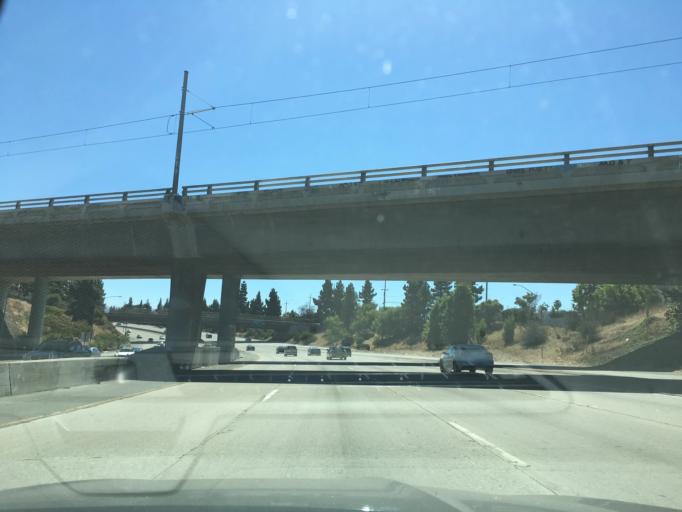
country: US
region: California
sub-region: Santa Clara County
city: Buena Vista
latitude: 37.3149
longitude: -121.9140
